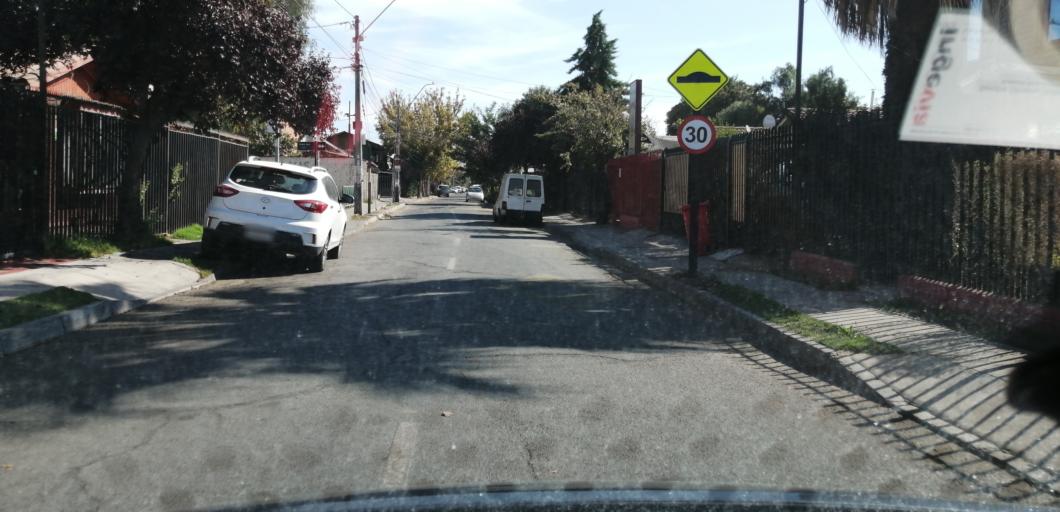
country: CL
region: Santiago Metropolitan
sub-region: Provincia de Santiago
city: Lo Prado
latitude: -33.4596
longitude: -70.7324
